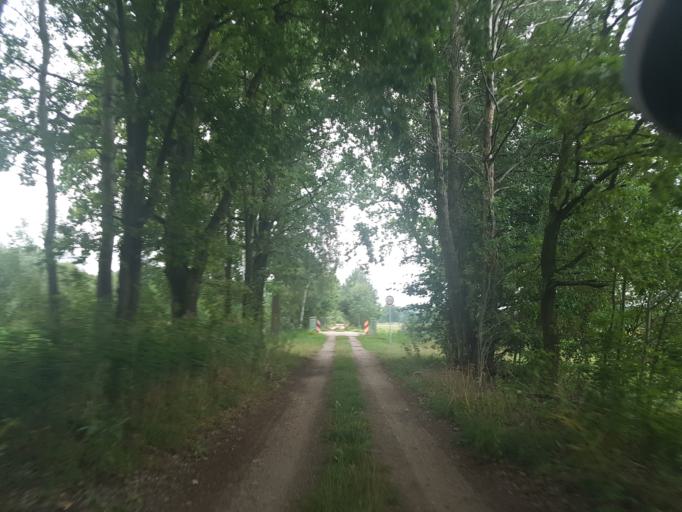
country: DE
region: Brandenburg
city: Finsterwalde
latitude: 51.6018
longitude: 13.6510
